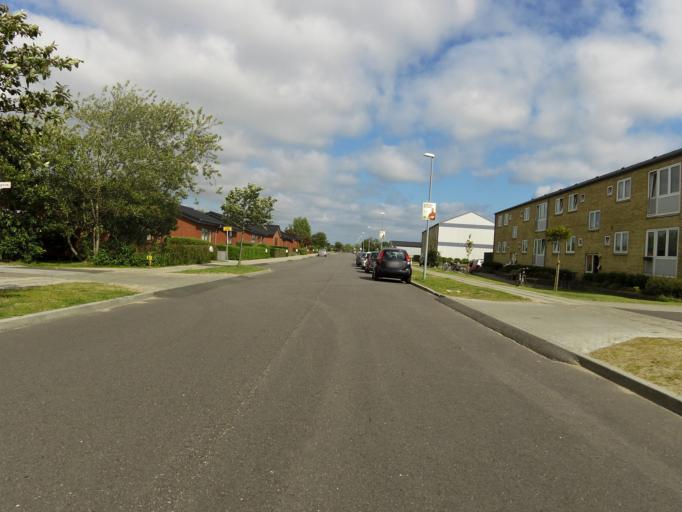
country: DK
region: South Denmark
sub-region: Esbjerg Kommune
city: Ribe
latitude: 55.3301
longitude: 8.7807
